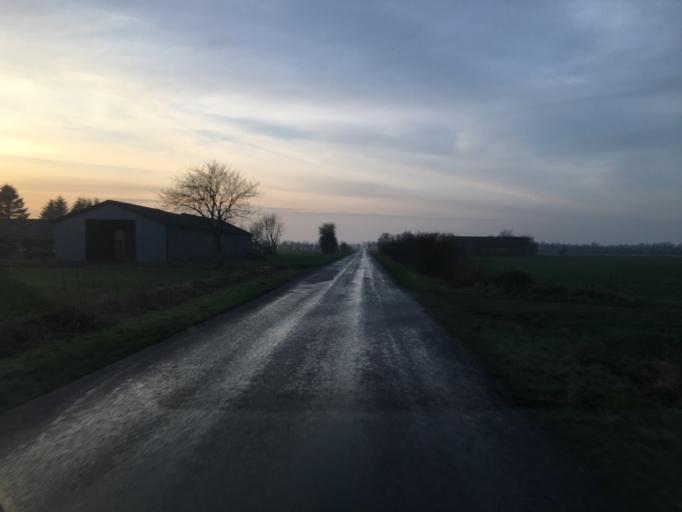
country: DK
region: South Denmark
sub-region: Tonder Kommune
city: Logumkloster
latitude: 55.1109
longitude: 9.0046
